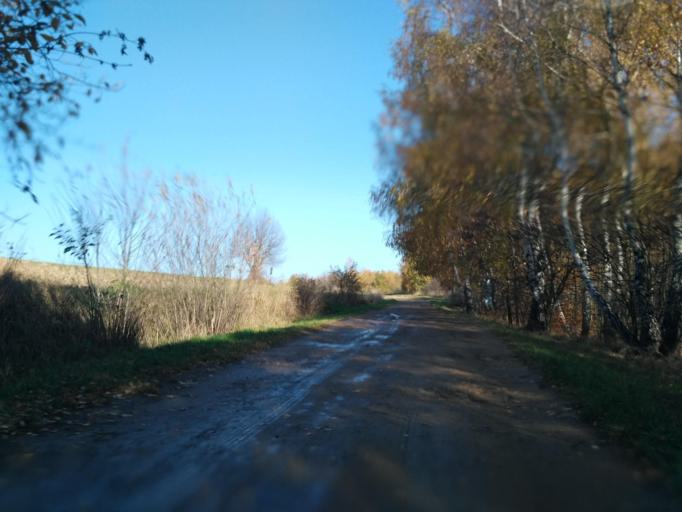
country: PL
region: Subcarpathian Voivodeship
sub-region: Powiat rzeszowski
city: Blazowa
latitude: 49.8649
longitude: 22.0844
